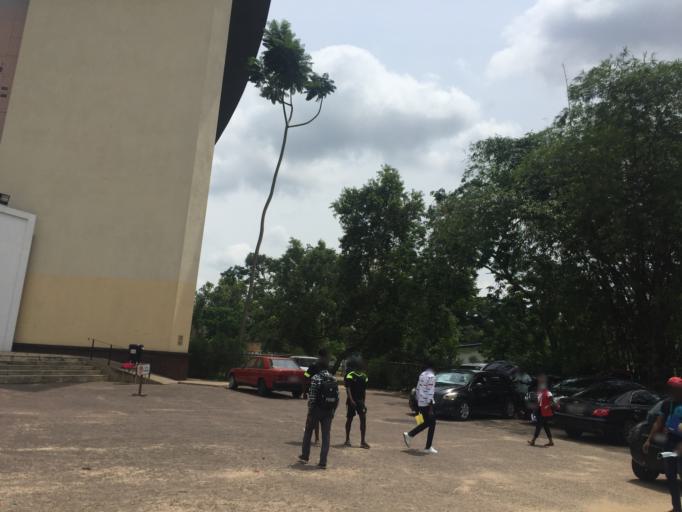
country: CD
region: Kinshasa
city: Masina
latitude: -4.4215
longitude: 15.3092
